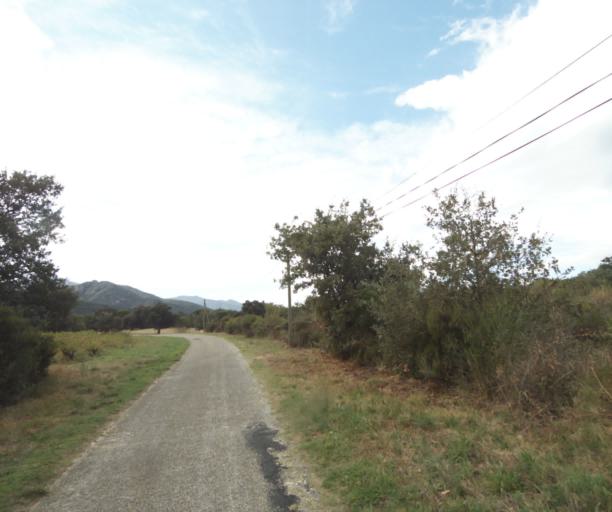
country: FR
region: Languedoc-Roussillon
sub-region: Departement des Pyrenees-Orientales
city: Argelers
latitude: 42.5371
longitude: 3.0075
